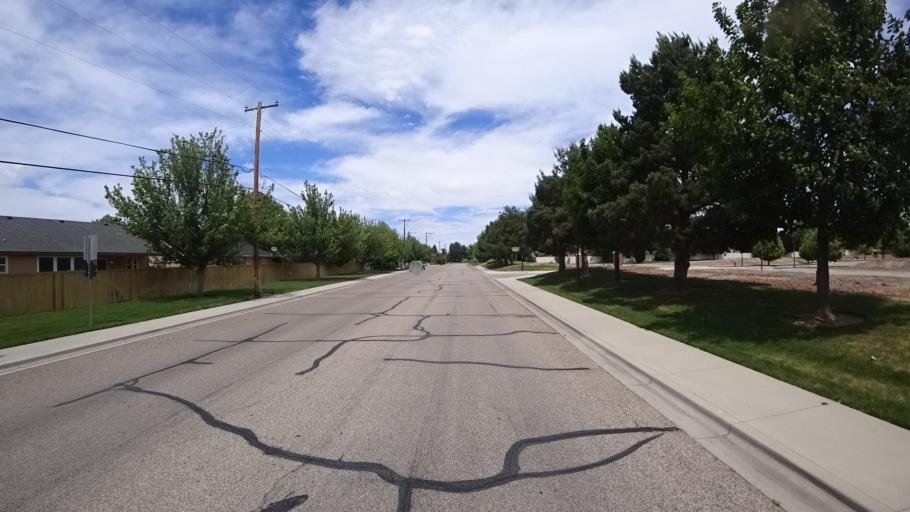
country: US
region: Idaho
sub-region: Ada County
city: Meridian
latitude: 43.6214
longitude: -116.3243
